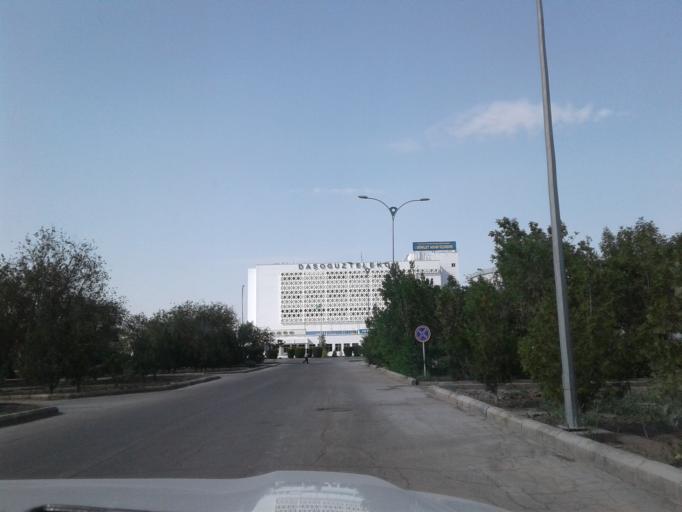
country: TM
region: Dasoguz
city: Dasoguz
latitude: 41.8336
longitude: 59.9648
